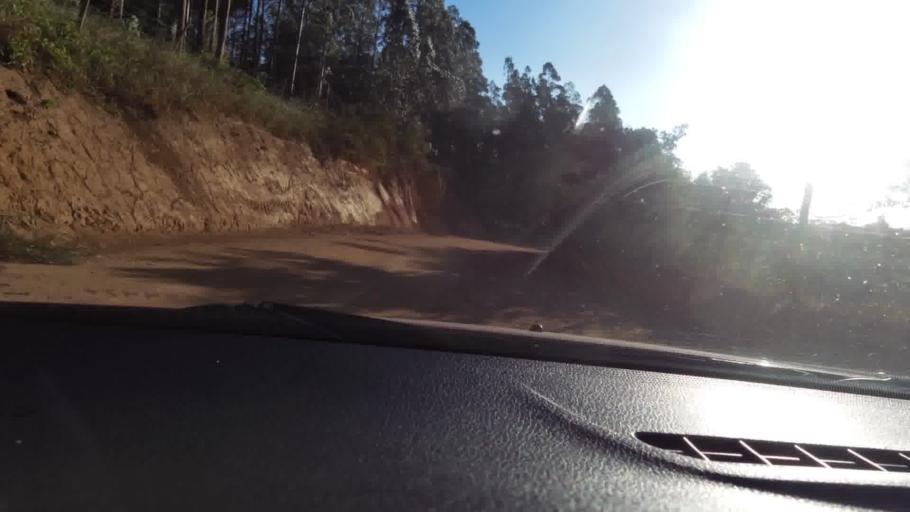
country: BR
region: Espirito Santo
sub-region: Guarapari
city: Guarapari
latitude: -20.5443
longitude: -40.4285
